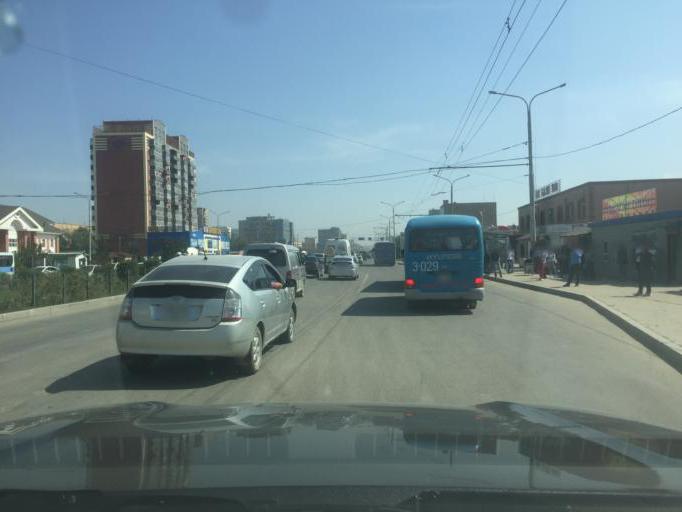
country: MN
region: Ulaanbaatar
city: Ulaanbaatar
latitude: 47.9097
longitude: 106.8143
